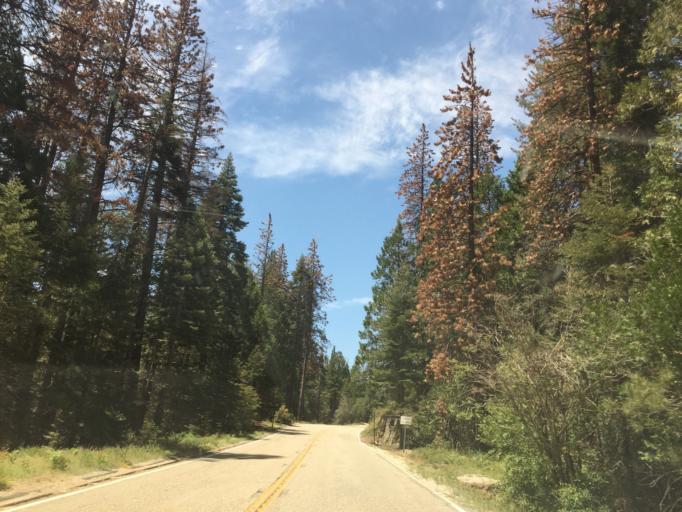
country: US
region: California
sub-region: Fresno County
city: Squaw Valley
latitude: 36.8056
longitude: -118.9424
